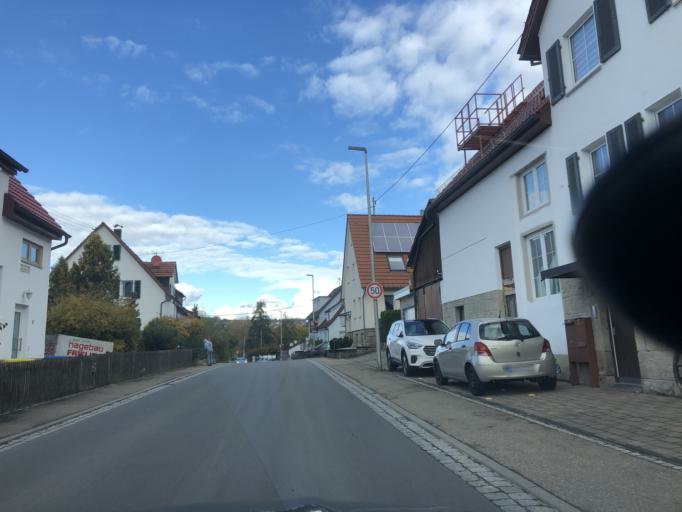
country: DE
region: Baden-Wuerttemberg
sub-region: Regierungsbezirk Stuttgart
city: Winterbach
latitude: 48.8435
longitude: 9.4537
